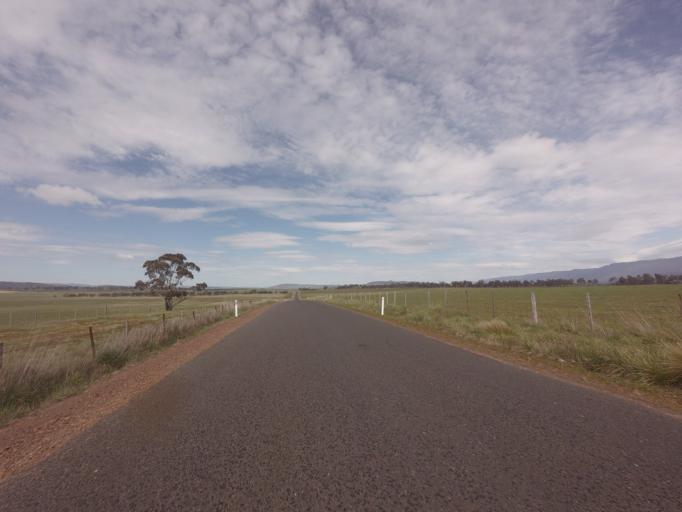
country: AU
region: Tasmania
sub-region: Northern Midlands
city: Evandale
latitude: -41.7911
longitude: 147.2486
